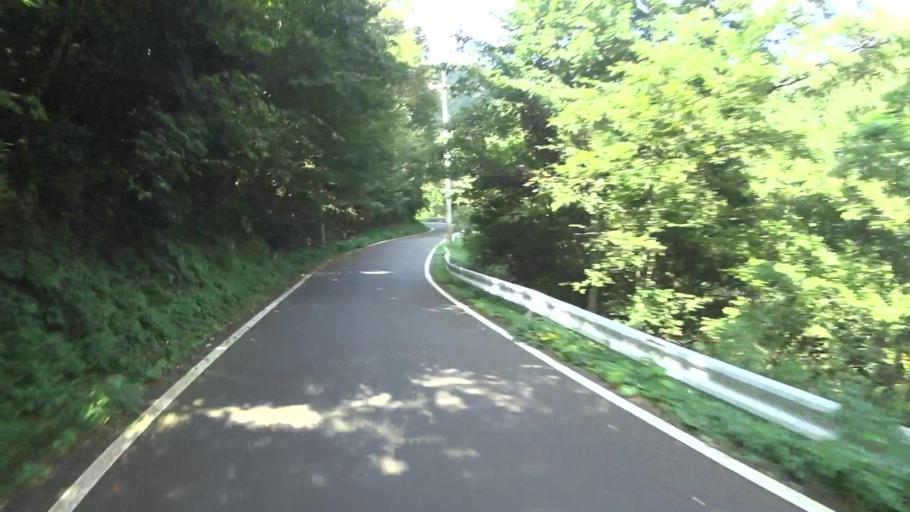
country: JP
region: Kyoto
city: Miyazu
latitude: 35.7279
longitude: 135.2074
